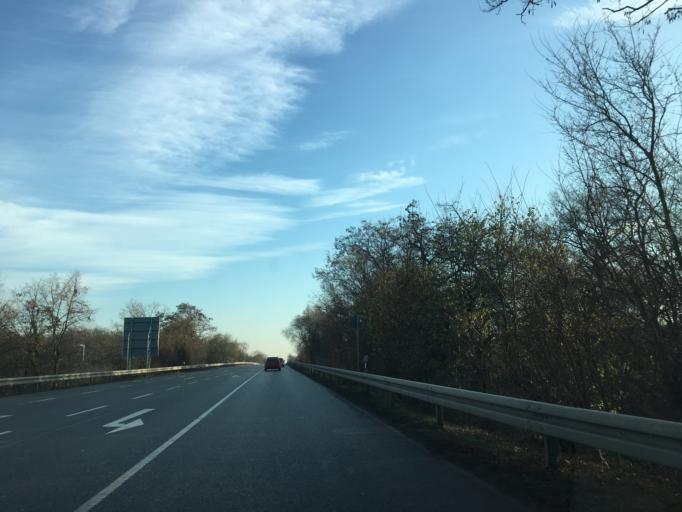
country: DE
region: Hesse
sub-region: Regierungsbezirk Darmstadt
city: Bischofsheim
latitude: 49.9745
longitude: 8.3793
